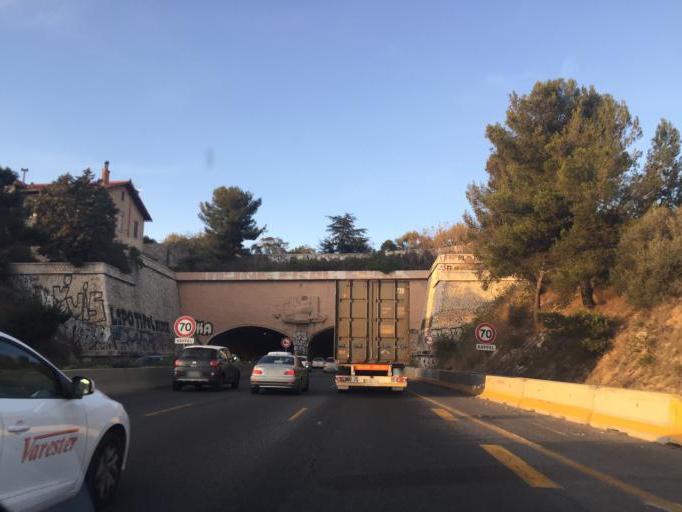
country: FR
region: Provence-Alpes-Cote d'Azur
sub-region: Departement des Bouches-du-Rhone
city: Marseille 15
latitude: 43.3667
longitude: 5.3609
